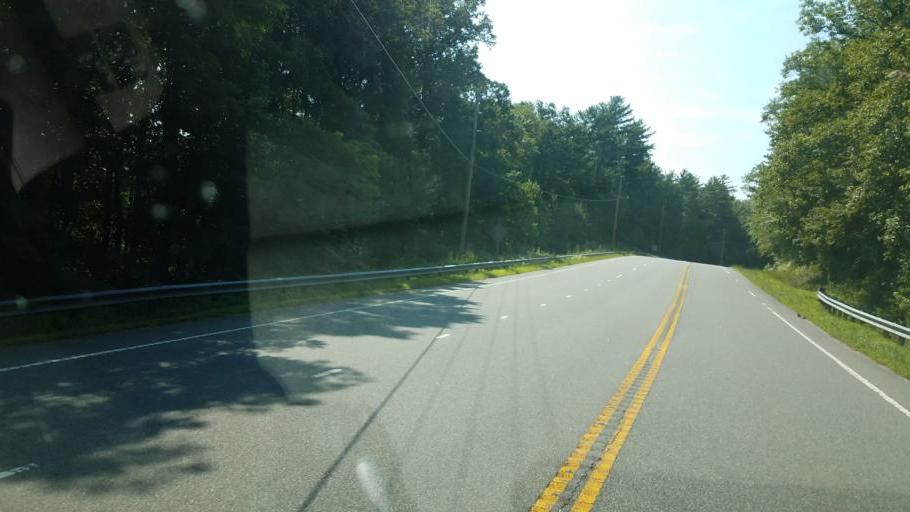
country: US
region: North Carolina
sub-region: Burke County
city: Glen Alpine
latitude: 35.8781
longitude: -81.7946
